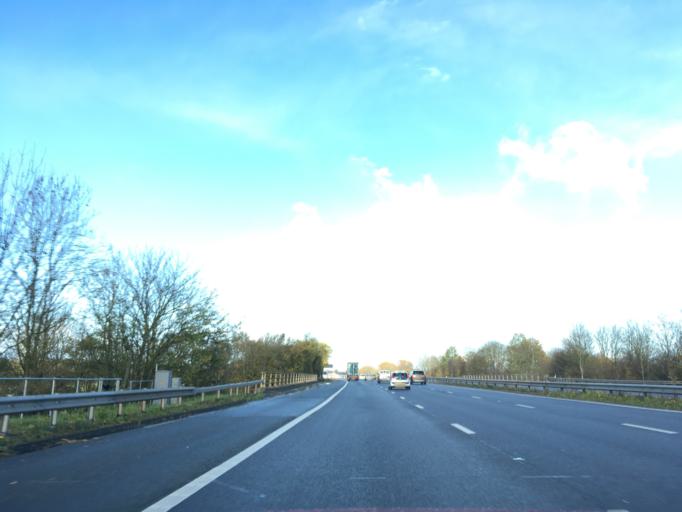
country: GB
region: England
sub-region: Worcestershire
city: Bredon
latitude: 52.0236
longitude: -2.1216
